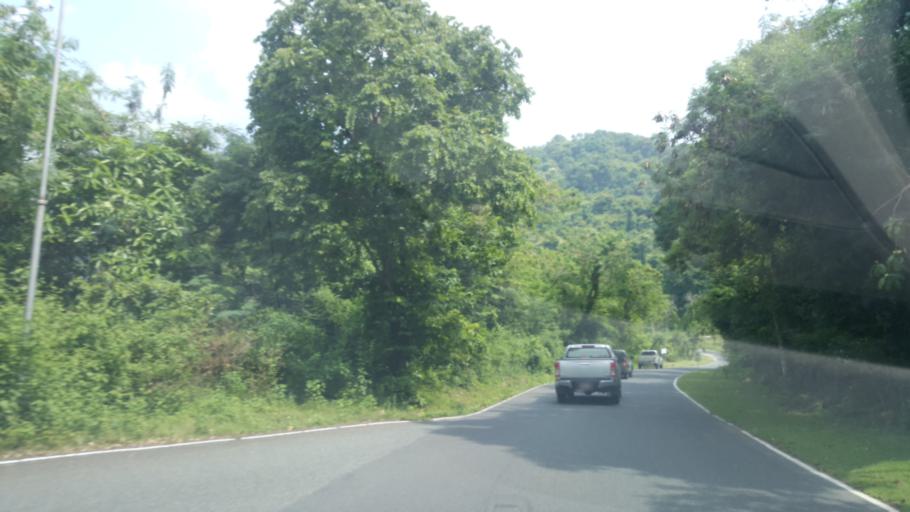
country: TH
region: Chon Buri
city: Ban Bueng
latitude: 13.2102
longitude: 101.0548
